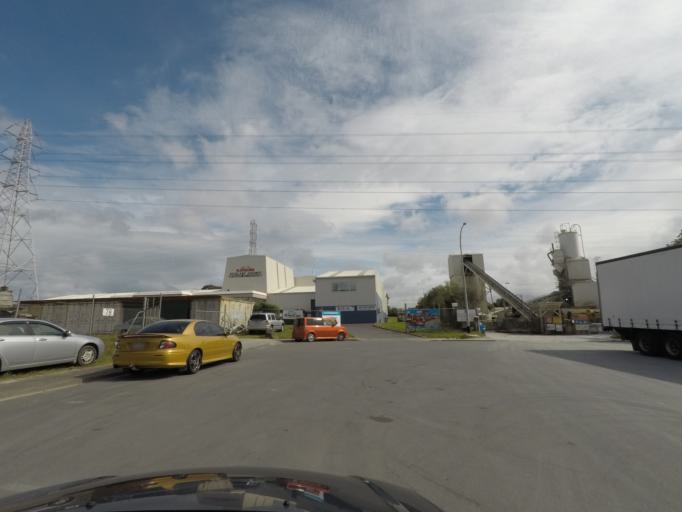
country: NZ
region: Auckland
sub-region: Auckland
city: Rosebank
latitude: -36.8507
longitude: 174.6398
